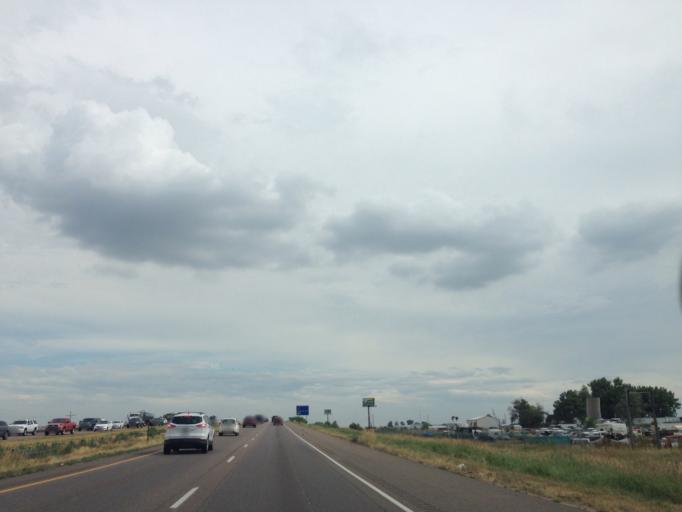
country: US
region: Colorado
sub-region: Weld County
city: Johnstown
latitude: 40.3524
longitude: -104.9819
